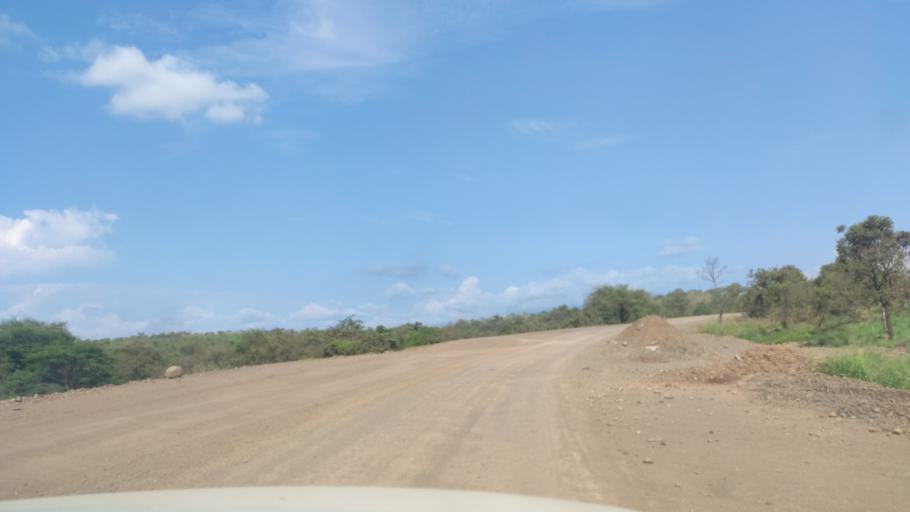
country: ET
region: Southern Nations, Nationalities, and People's Region
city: Felege Neway
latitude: 6.4291
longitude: 37.2110
